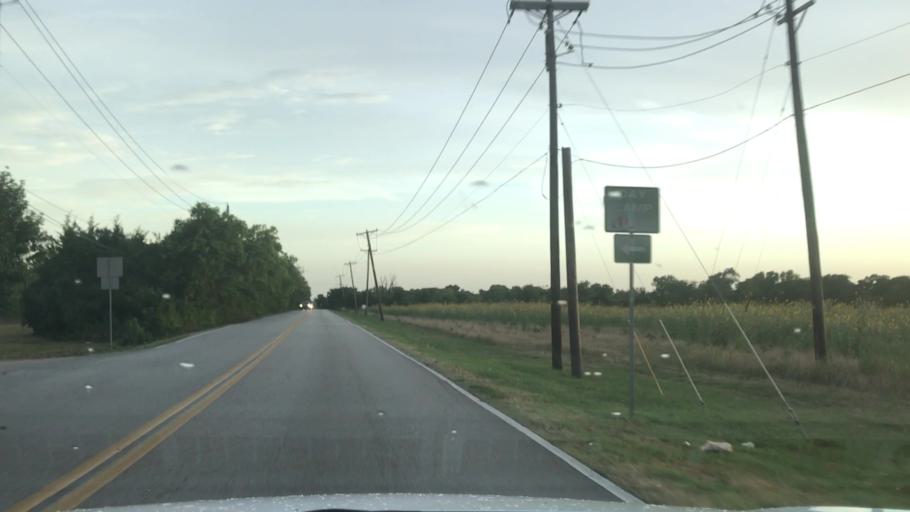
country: US
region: Texas
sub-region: Dallas County
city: Mesquite
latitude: 32.7196
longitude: -96.5443
